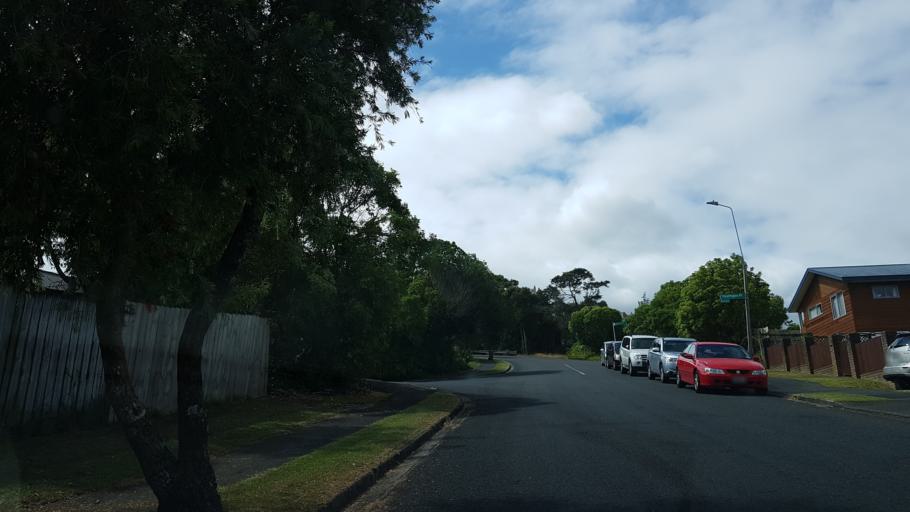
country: NZ
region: Auckland
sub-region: Auckland
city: North Shore
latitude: -36.7808
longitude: 174.7093
